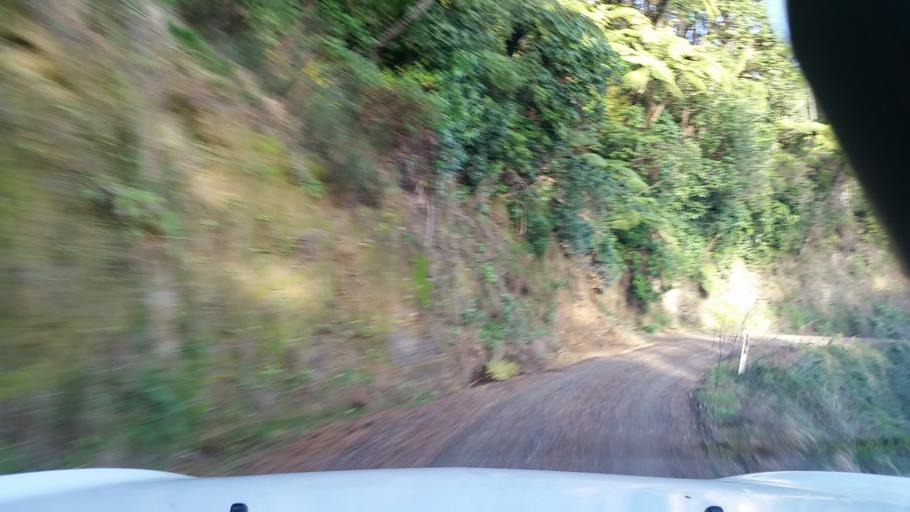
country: NZ
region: Taranaki
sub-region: New Plymouth District
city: Waitara
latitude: -38.9070
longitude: 174.5089
